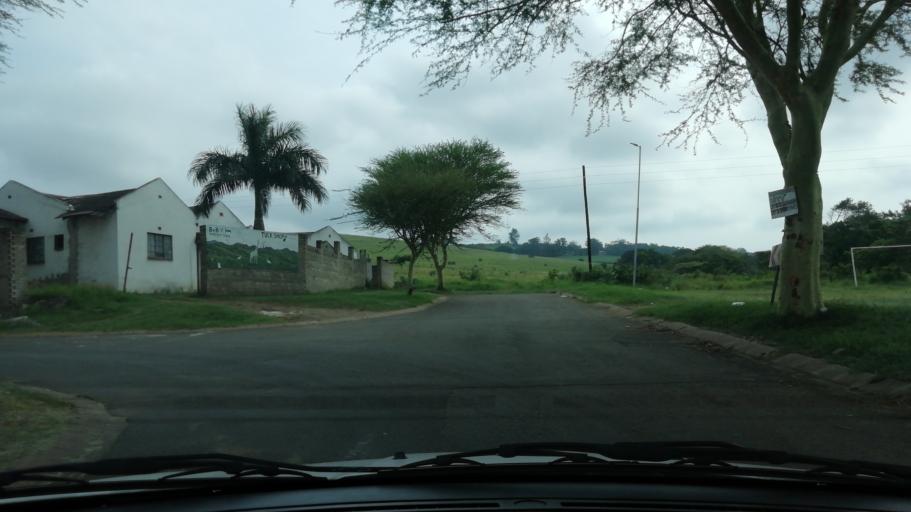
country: ZA
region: KwaZulu-Natal
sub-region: uThungulu District Municipality
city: Empangeni
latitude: -28.7360
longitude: 31.8765
